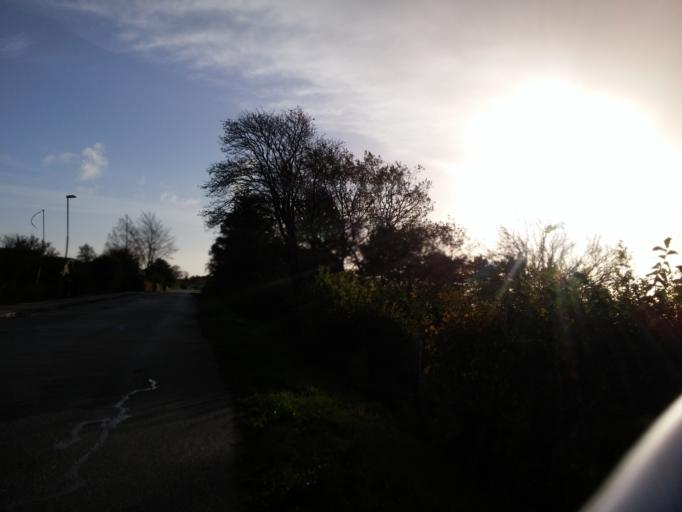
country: DK
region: South Denmark
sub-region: Kerteminde Kommune
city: Kerteminde
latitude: 55.4520
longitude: 10.6437
